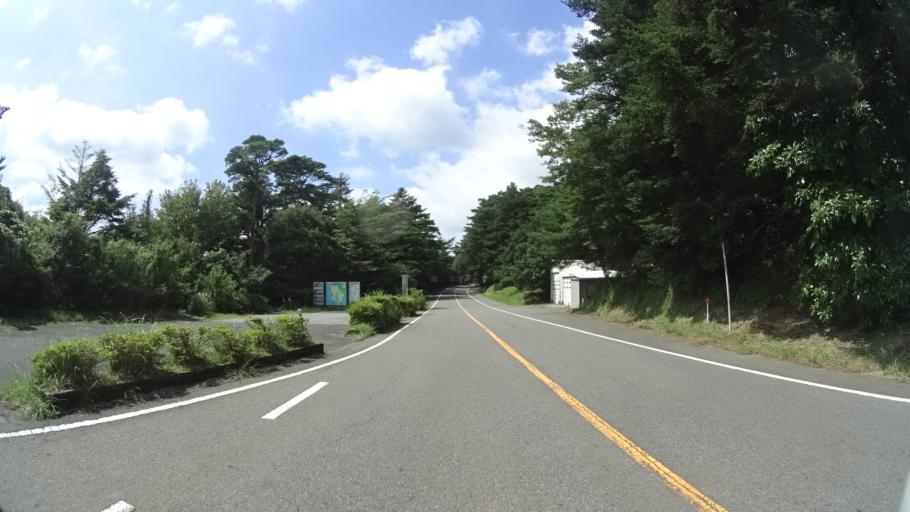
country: JP
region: Miyazaki
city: Kobayashi
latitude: 31.8994
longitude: 130.8515
